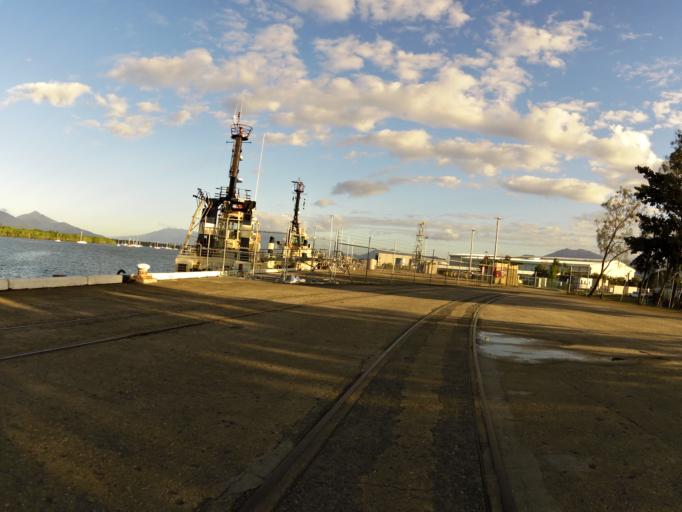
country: AU
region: Queensland
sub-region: Cairns
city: Cairns
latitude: -16.9283
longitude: 145.7798
